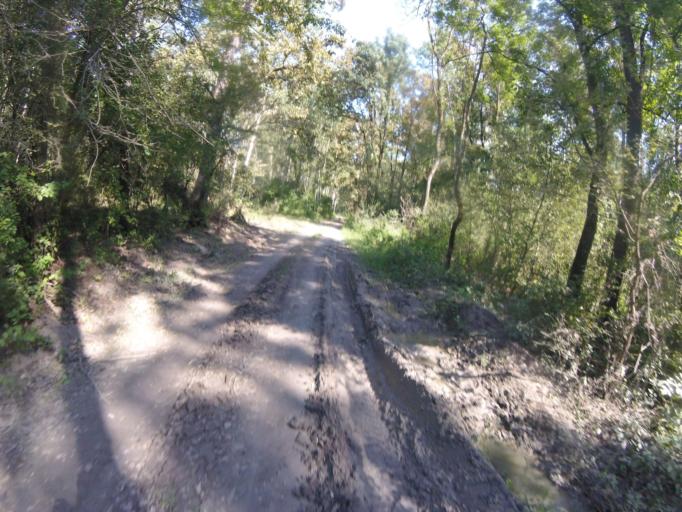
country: HU
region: Bacs-Kiskun
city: Baja
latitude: 46.2008
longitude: 18.8520
